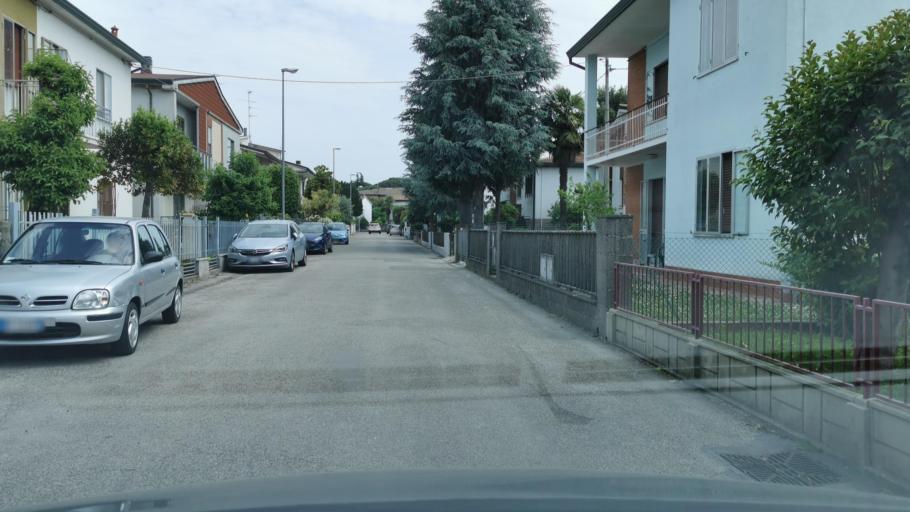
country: IT
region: Emilia-Romagna
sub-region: Provincia di Ravenna
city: Bagnacavallo
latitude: 44.4149
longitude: 11.9705
